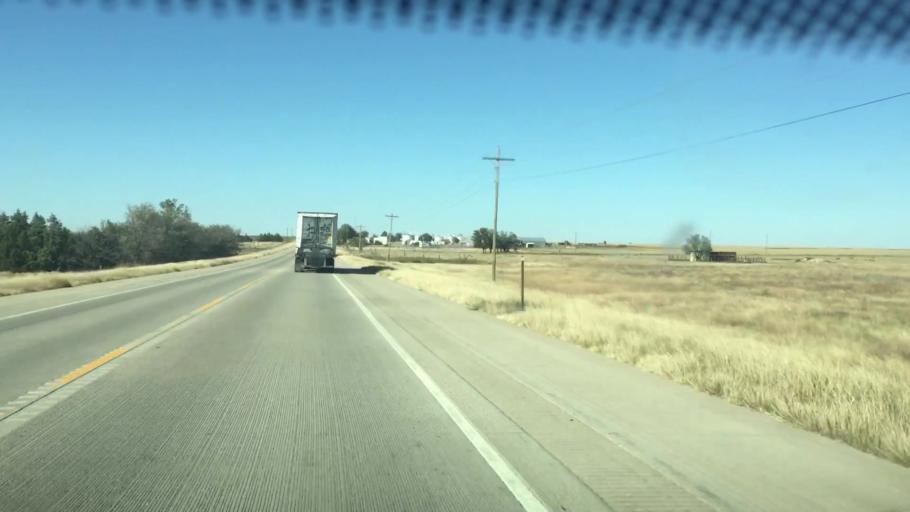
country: US
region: Colorado
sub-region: Kiowa County
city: Eads
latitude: 38.4588
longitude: -102.7306
